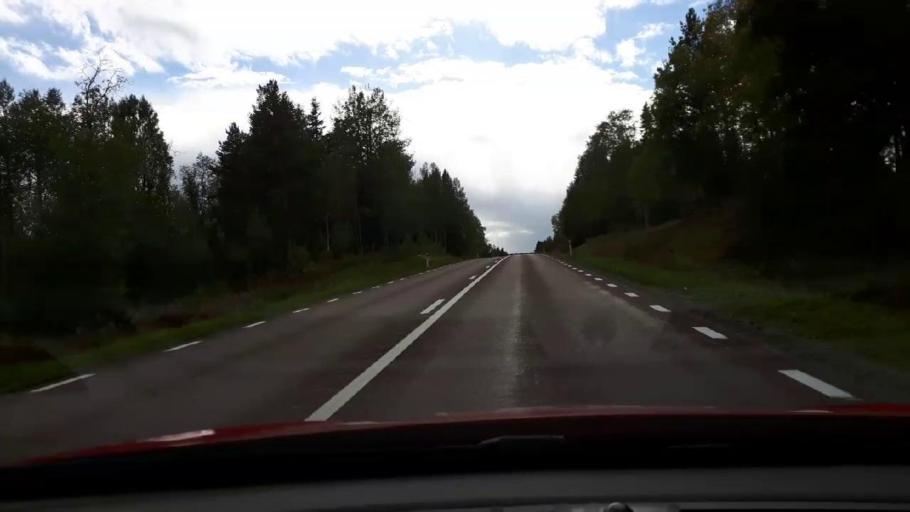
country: SE
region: Jaemtland
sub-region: OEstersunds Kommun
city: Brunflo
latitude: 63.0225
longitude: 14.7481
